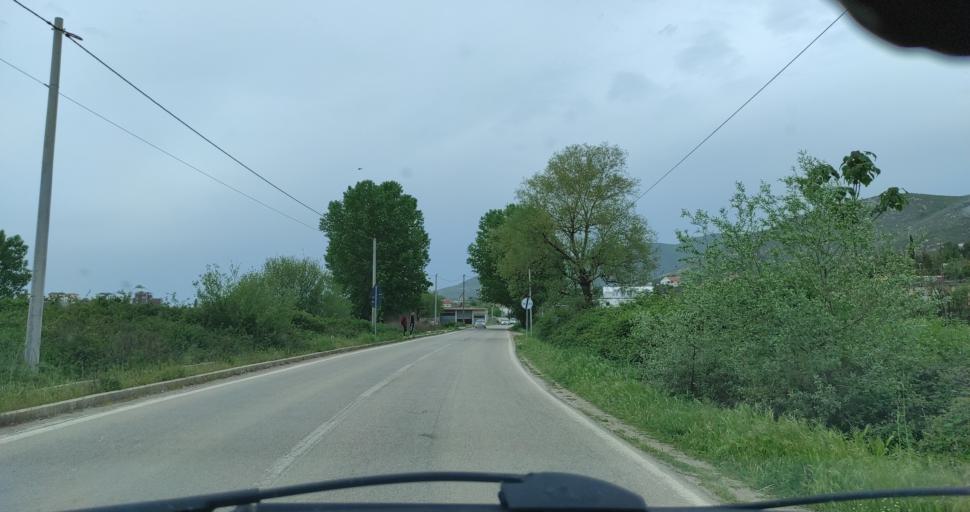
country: AL
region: Lezhe
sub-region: Rrethi i Kurbinit
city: Lac
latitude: 41.6137
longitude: 19.7113
